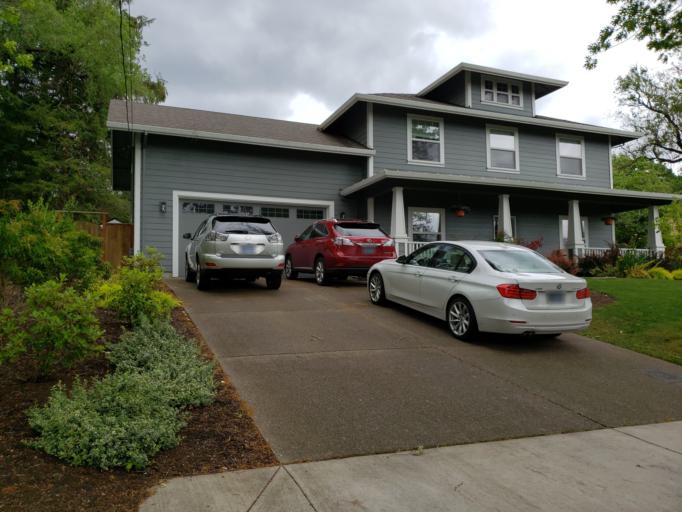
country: US
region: Oregon
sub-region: Washington County
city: Raleigh Hills
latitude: 45.4787
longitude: -122.7379
